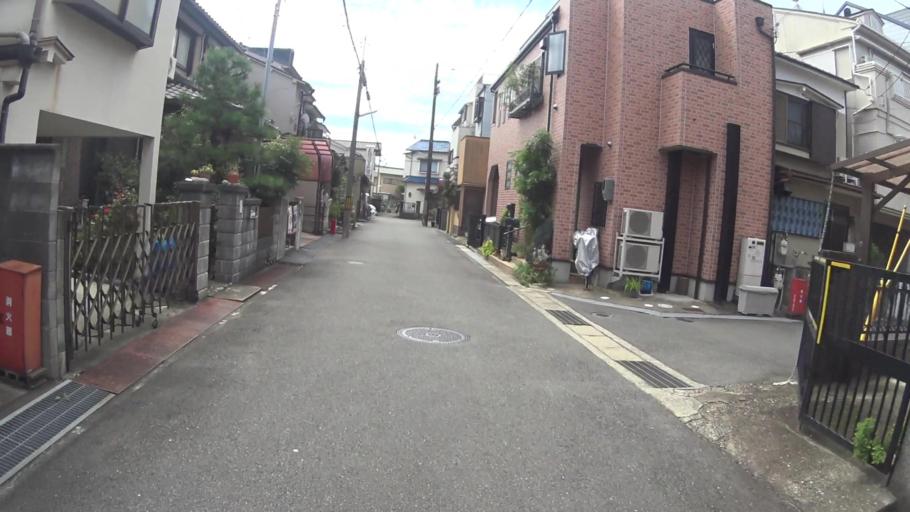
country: JP
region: Kyoto
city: Muko
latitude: 34.9546
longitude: 135.7070
